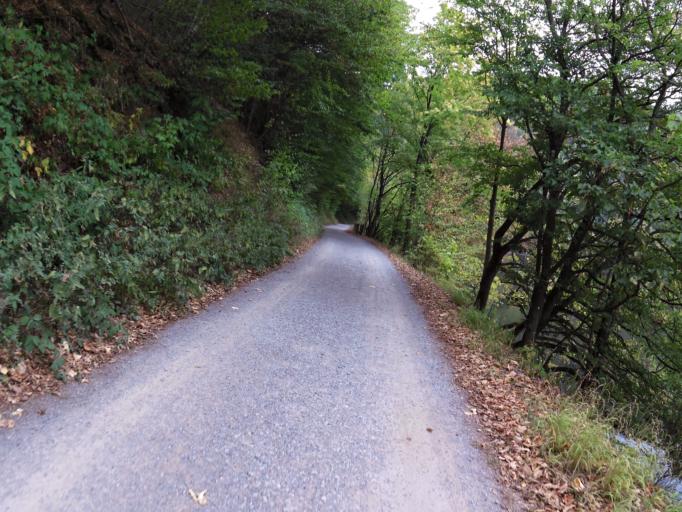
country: DE
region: North Rhine-Westphalia
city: Heimbach
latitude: 50.6078
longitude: 6.4156
